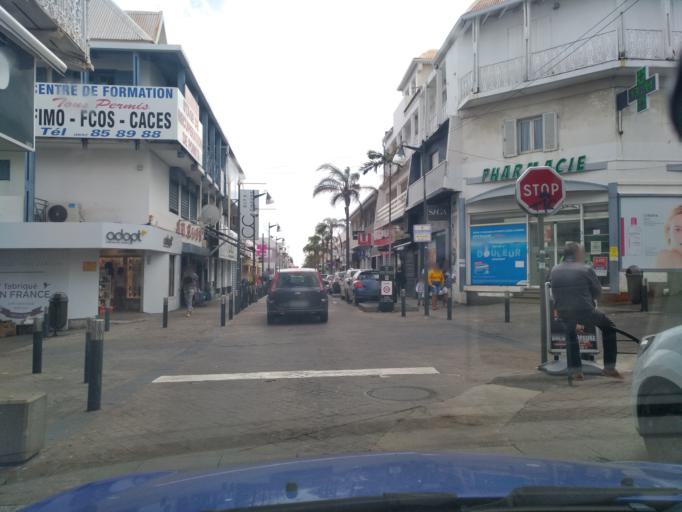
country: RE
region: Reunion
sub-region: Reunion
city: Saint-Pierre
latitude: -21.3399
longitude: 55.4744
